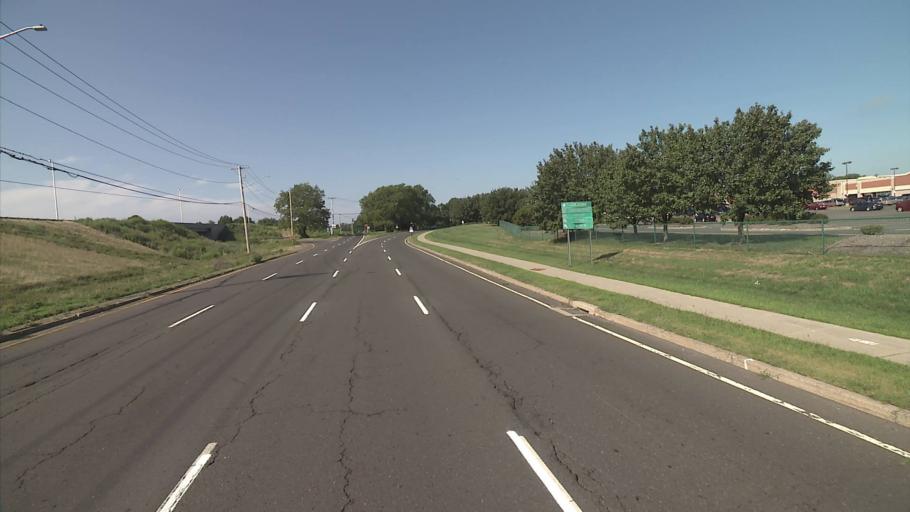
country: US
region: Connecticut
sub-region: Fairfield County
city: Stratford
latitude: 41.1999
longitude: -73.1176
